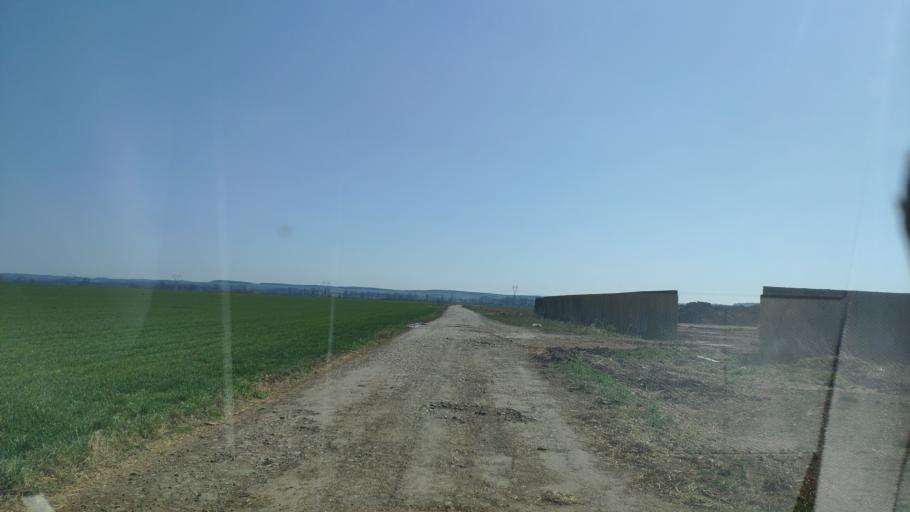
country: SK
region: Kosicky
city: Moldava nad Bodvou
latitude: 48.5973
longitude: 20.9551
